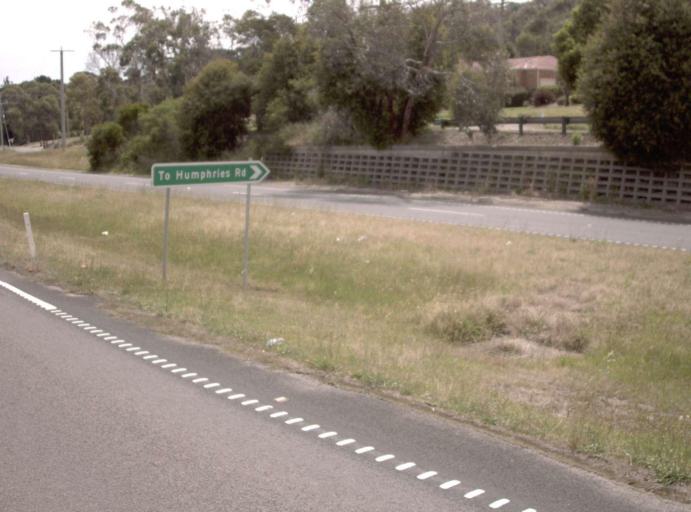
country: AU
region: Victoria
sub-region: Mornington Peninsula
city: Moorooduc
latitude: -38.2000
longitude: 145.1291
